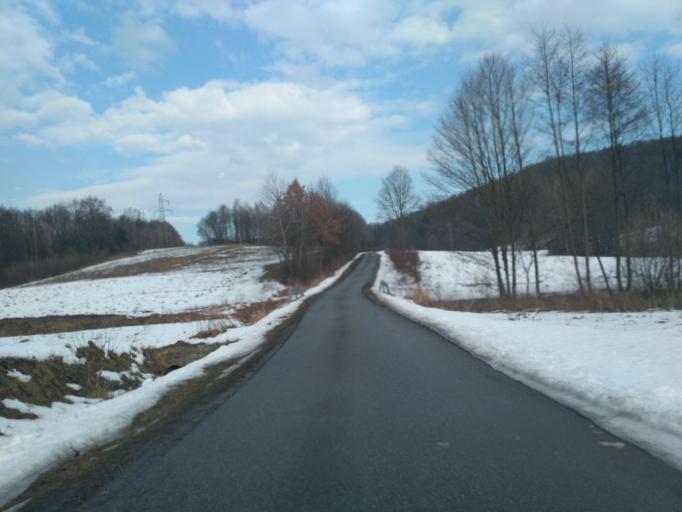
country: PL
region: Subcarpathian Voivodeship
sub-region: Powiat brzozowski
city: Niebocko
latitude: 49.6448
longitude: 22.1302
